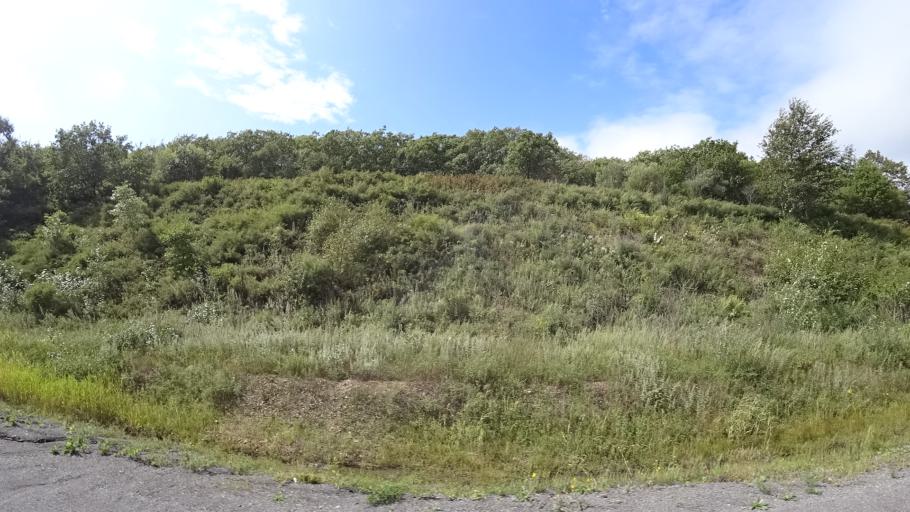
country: RU
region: Primorskiy
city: Lyalichi
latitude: 44.1302
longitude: 132.4268
